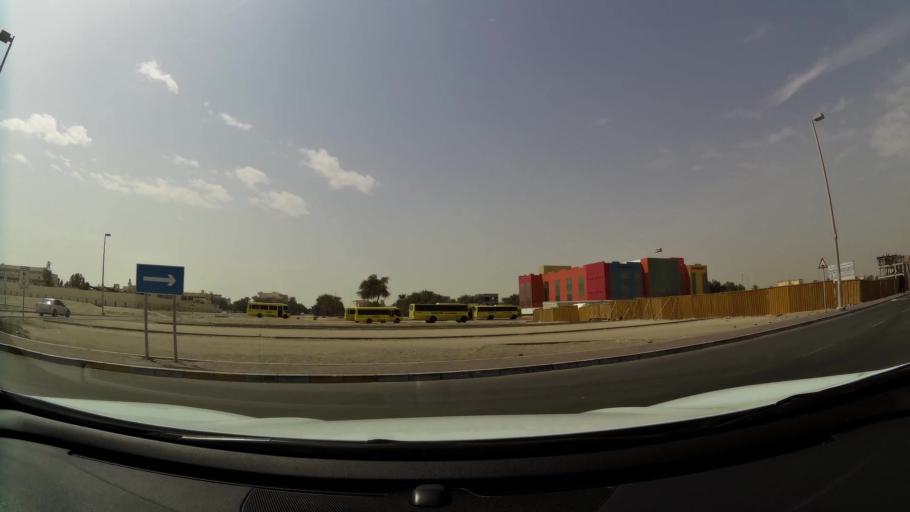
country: AE
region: Abu Dhabi
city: Abu Dhabi
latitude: 24.2940
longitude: 54.6392
